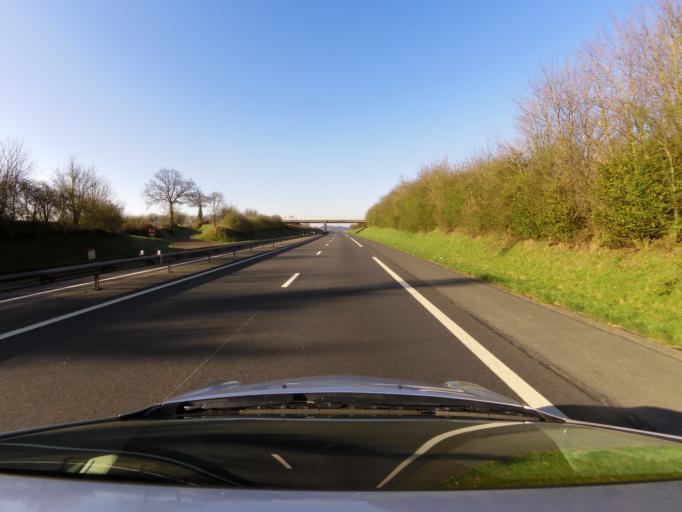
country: FR
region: Lower Normandy
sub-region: Departement du Calvados
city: Saint-Martin-des-Besaces
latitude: 49.0023
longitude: -0.9085
